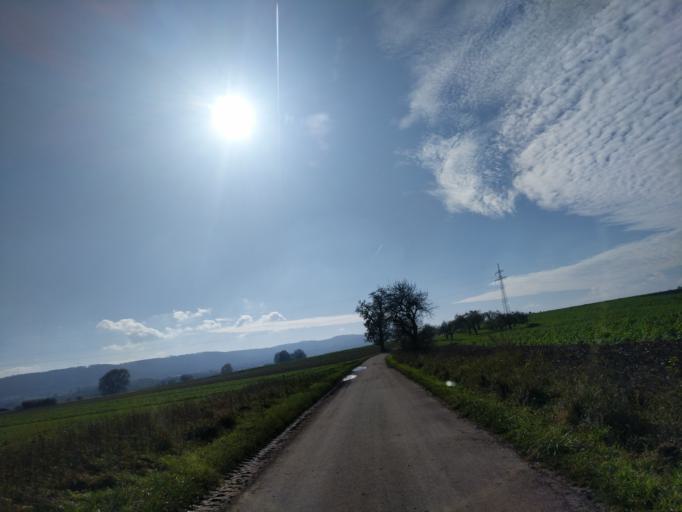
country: DE
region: Baden-Wuerttemberg
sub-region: Tuebingen Region
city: Rottenburg
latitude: 48.4983
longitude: 8.9583
